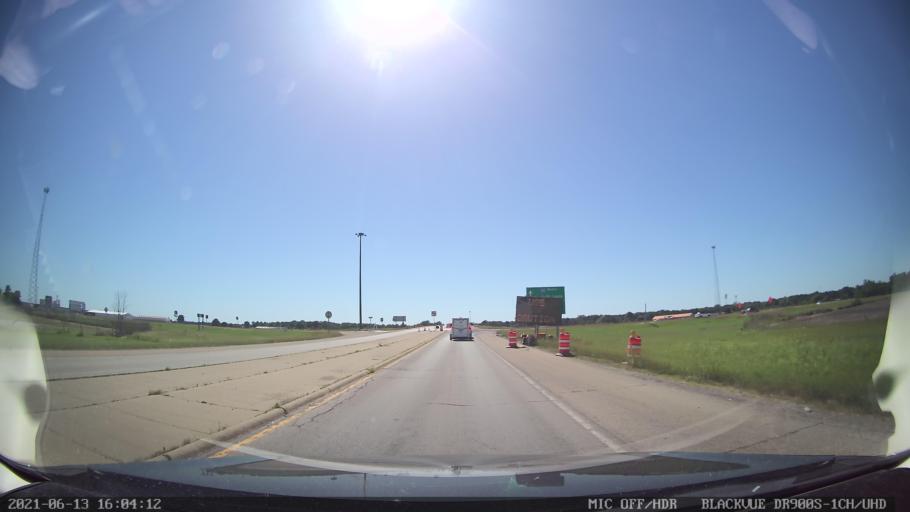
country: US
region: Illinois
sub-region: Montgomery County
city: Raymond
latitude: 39.2779
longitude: -89.6380
